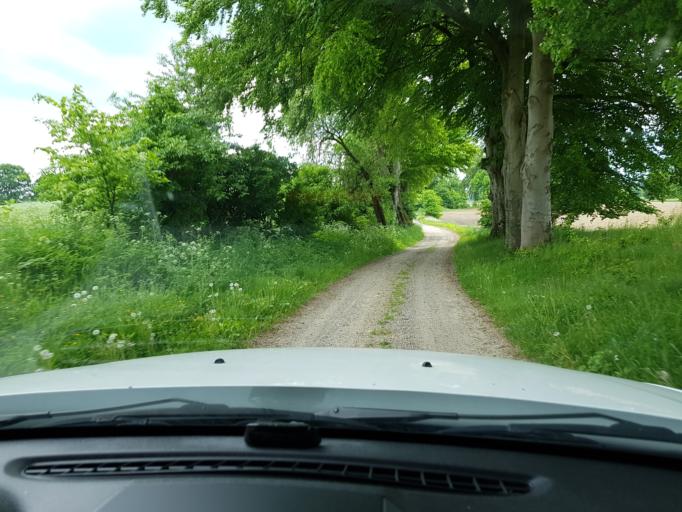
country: PL
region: West Pomeranian Voivodeship
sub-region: Powiat drawski
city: Drawsko Pomorskie
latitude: 53.5434
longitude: 15.7369
